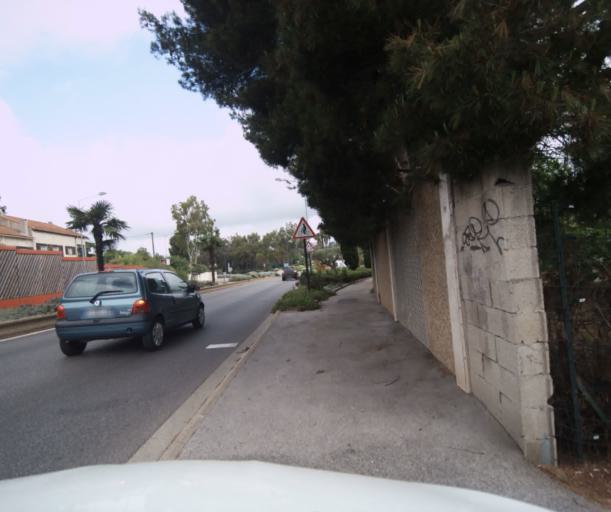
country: FR
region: Provence-Alpes-Cote d'Azur
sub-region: Departement du Var
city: Six-Fours-les-Plages
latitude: 43.1035
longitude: 5.8540
